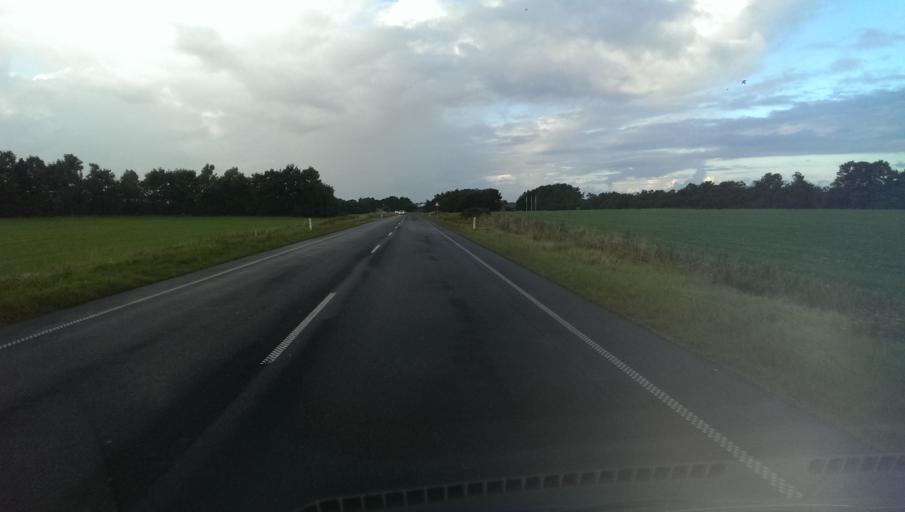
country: DK
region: South Denmark
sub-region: Varde Kommune
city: Olgod
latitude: 55.7910
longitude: 8.6267
